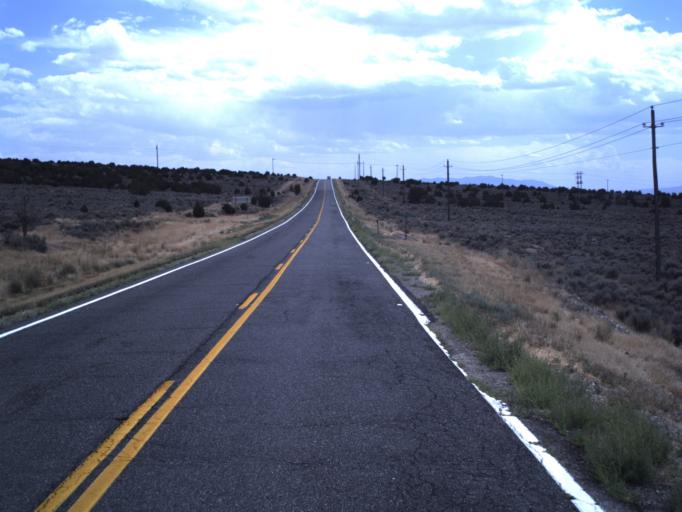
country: US
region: Utah
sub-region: Tooele County
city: Tooele
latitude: 40.3218
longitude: -112.2870
